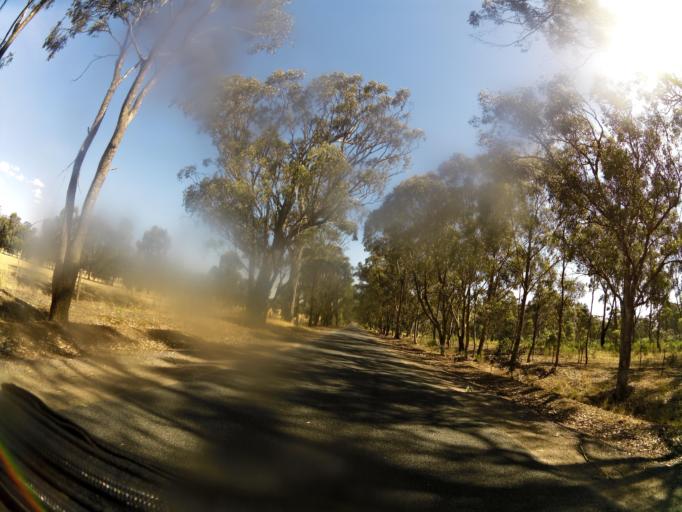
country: AU
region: Victoria
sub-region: Campaspe
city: Kyabram
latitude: -36.8715
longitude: 145.0863
